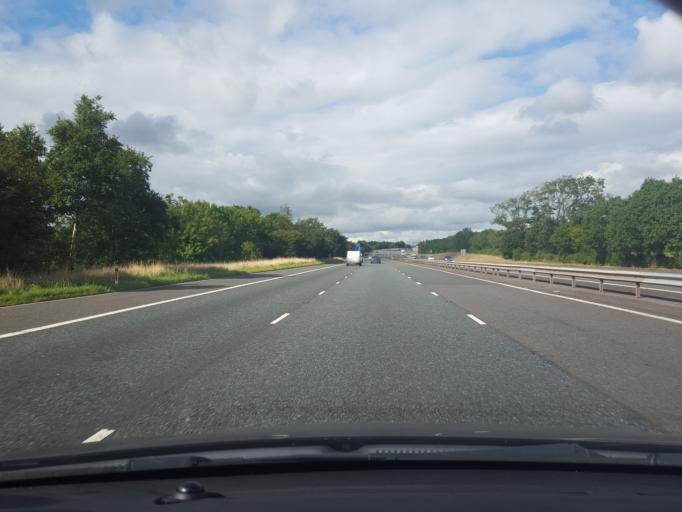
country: GB
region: Scotland
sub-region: Dumfries and Galloway
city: Gretna
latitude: 55.0151
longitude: -3.1082
